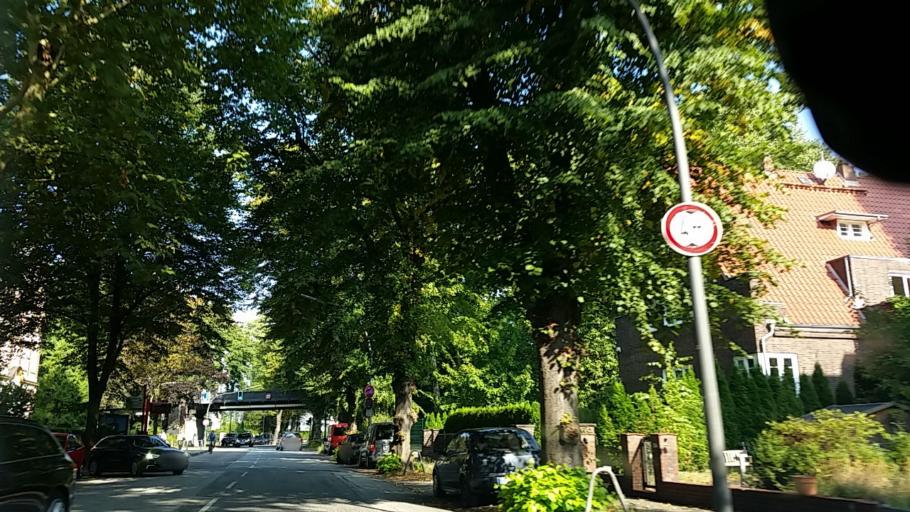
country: DE
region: Hamburg
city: Winterhude
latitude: 53.5897
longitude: 10.0034
